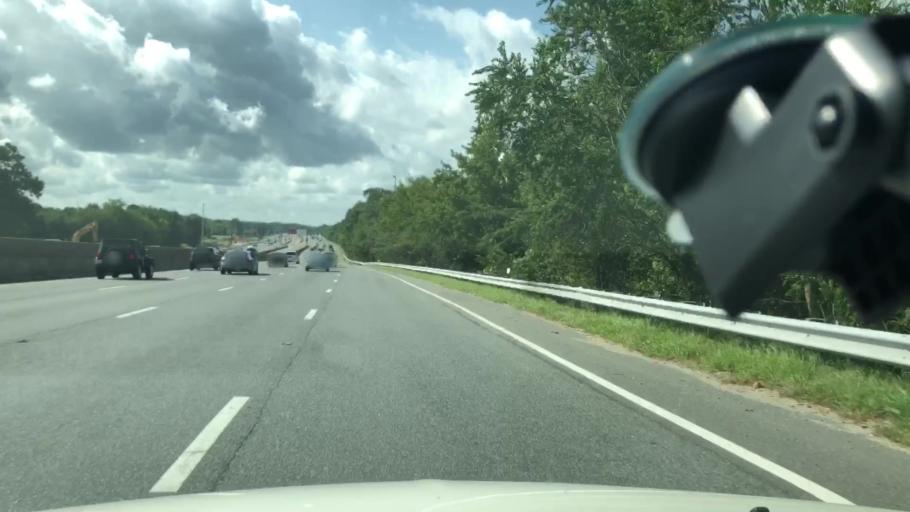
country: US
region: Virginia
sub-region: City of Chesapeake
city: Chesapeake
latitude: 36.8406
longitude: -76.1967
